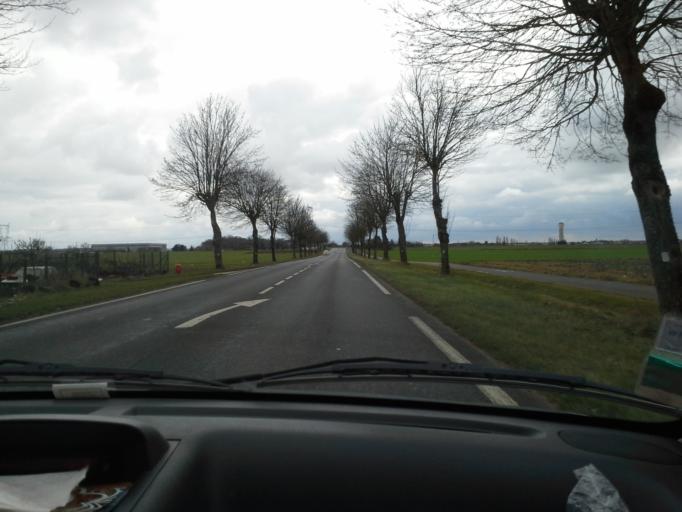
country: FR
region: Centre
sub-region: Departement du Loir-et-Cher
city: Saint-Sulpice-de-Pommeray
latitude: 47.6419
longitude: 1.2787
